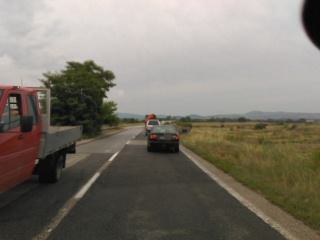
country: BG
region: Plovdiv
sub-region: Obshtina Karlovo
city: Karlovo
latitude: 42.5637
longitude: 24.8298
